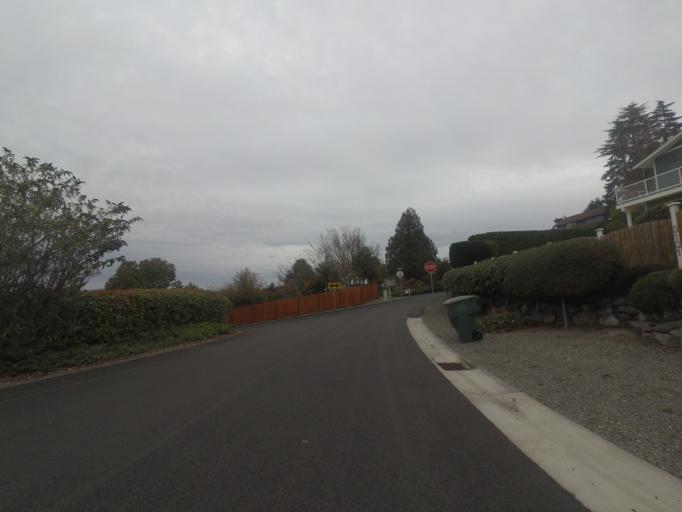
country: US
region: Washington
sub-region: Pierce County
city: University Place
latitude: 47.2320
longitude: -122.5618
